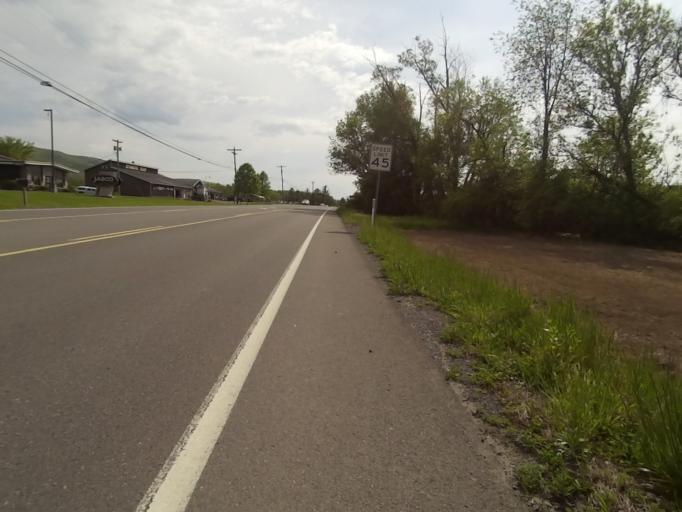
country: US
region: Pennsylvania
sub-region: Centre County
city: Pleasant Gap
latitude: 40.8590
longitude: -77.7602
